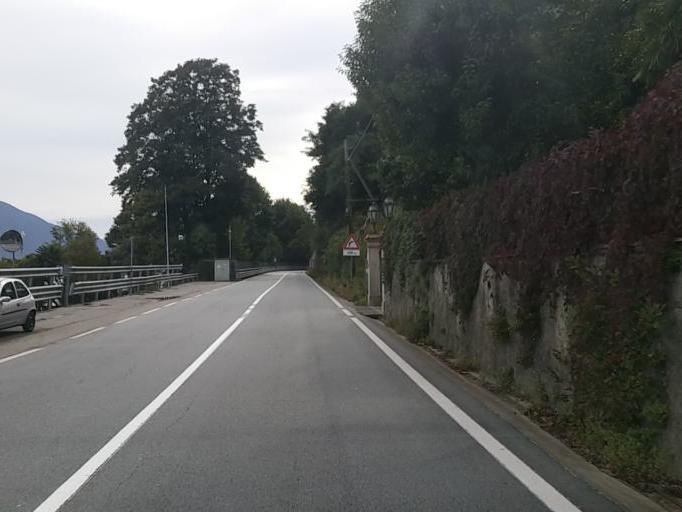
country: IT
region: Piedmont
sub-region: Provincia Verbano-Cusio-Ossola
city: Gonte
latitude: 45.9965
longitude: 8.6547
